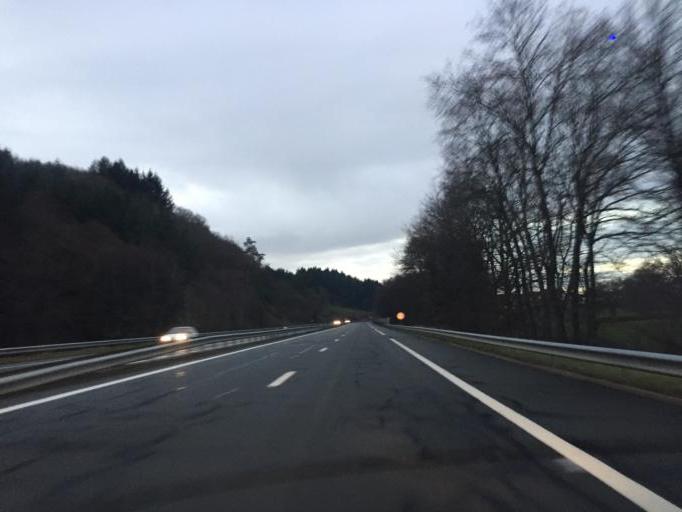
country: FR
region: Bourgogne
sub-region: Departement de Saone-et-Loire
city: Matour
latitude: 46.3744
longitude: 4.5364
